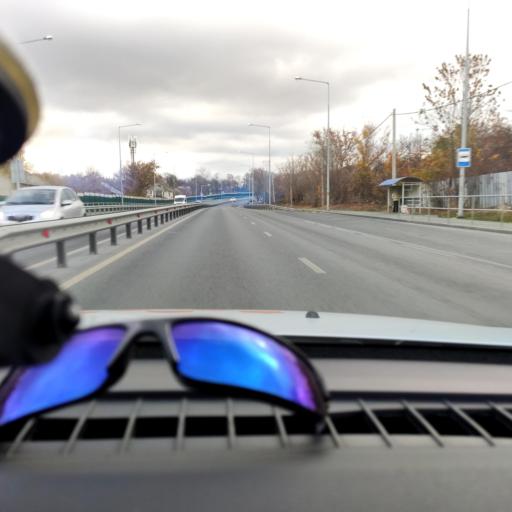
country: RU
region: Samara
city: Volzhskiy
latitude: 53.3657
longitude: 50.1972
